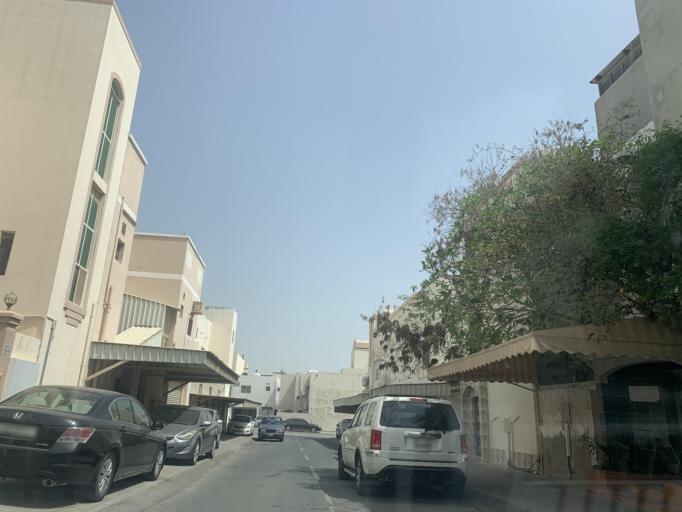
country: BH
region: Northern
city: Madinat `Isa
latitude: 26.1510
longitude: 50.5217
